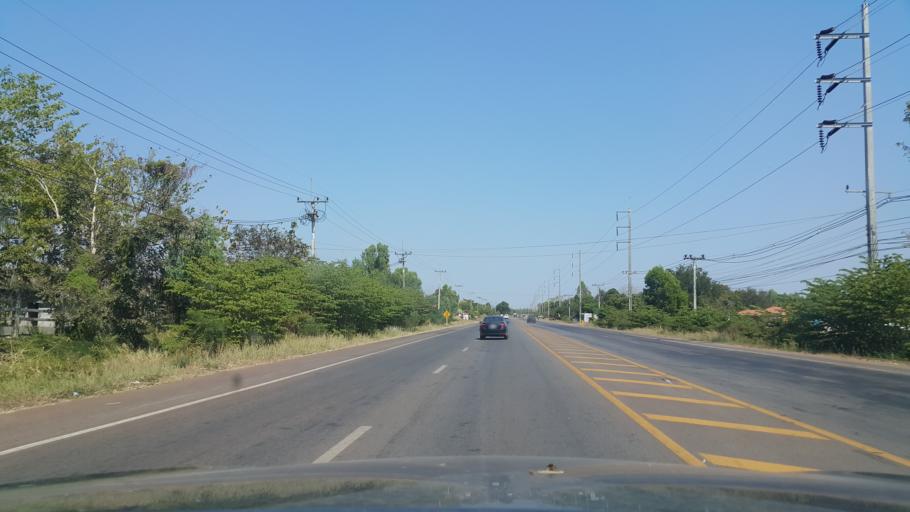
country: TH
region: Changwat Udon Thani
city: Nong Han
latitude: 17.3738
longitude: 103.1826
